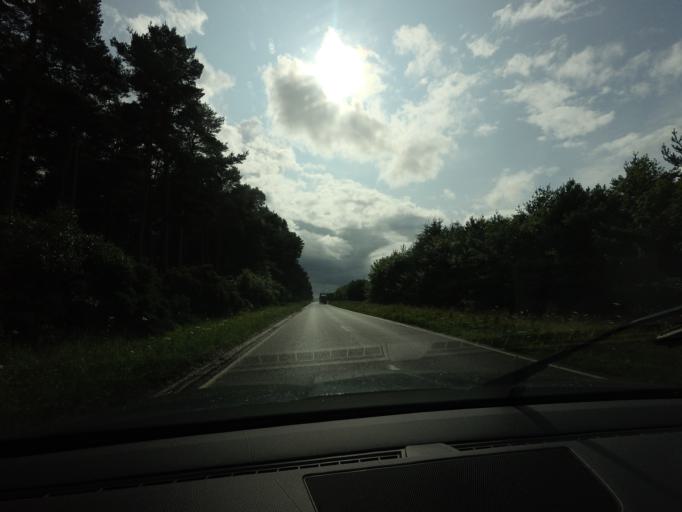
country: GB
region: Scotland
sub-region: Highland
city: Nairn
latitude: 57.5693
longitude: -3.9381
